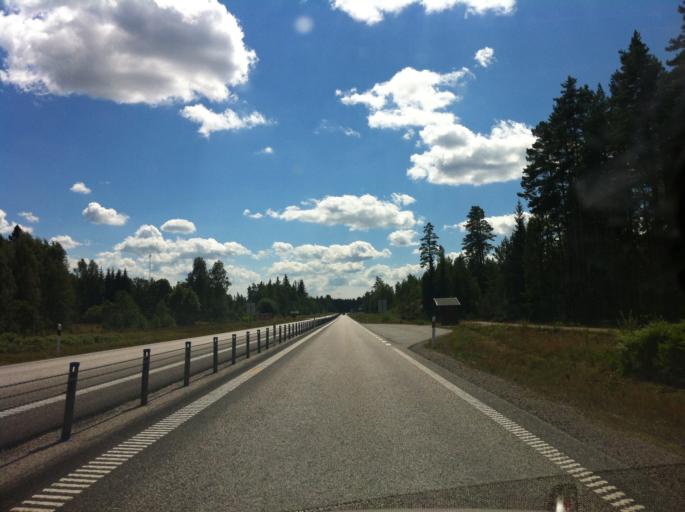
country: SE
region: Joenkoeping
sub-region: Gislaveds Kommun
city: Gislaved
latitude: 57.3377
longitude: 13.5493
